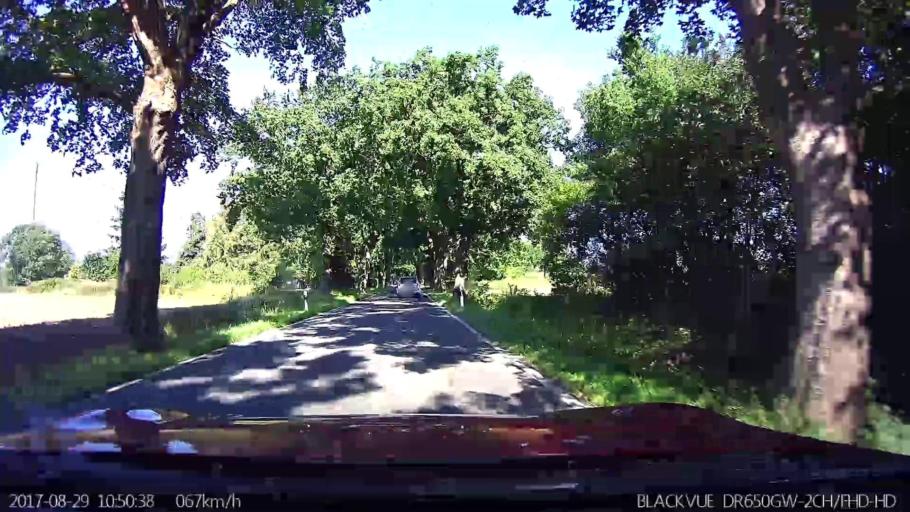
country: DE
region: Mecklenburg-Vorpommern
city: Velgast
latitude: 54.2618
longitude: 12.8206
